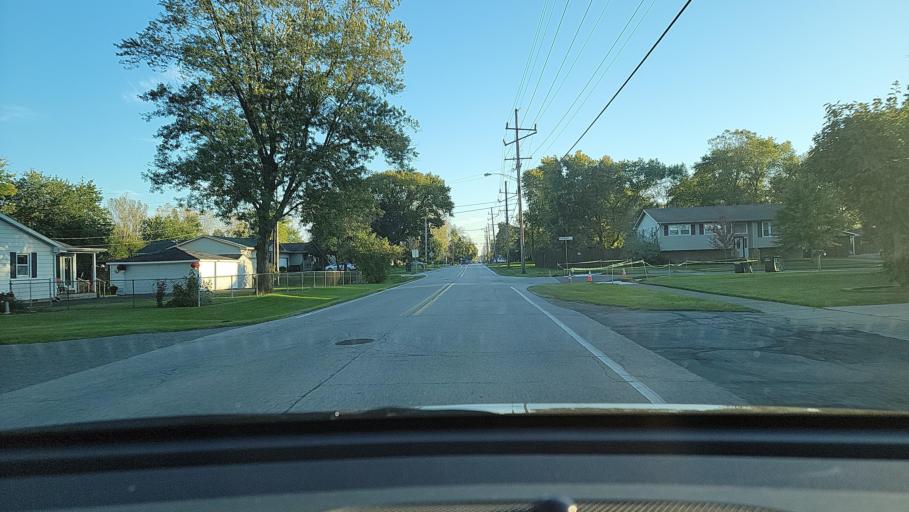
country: US
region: Indiana
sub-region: Porter County
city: Portage
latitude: 41.5604
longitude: -87.1974
